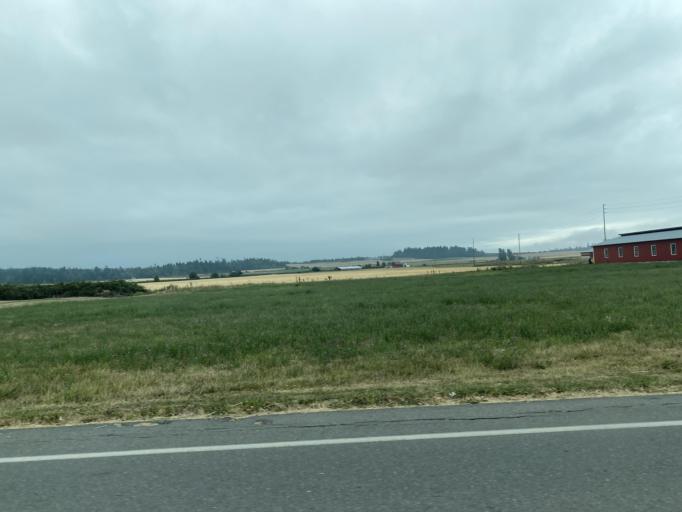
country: US
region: Washington
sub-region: Island County
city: Coupeville
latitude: 48.2039
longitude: -122.6938
